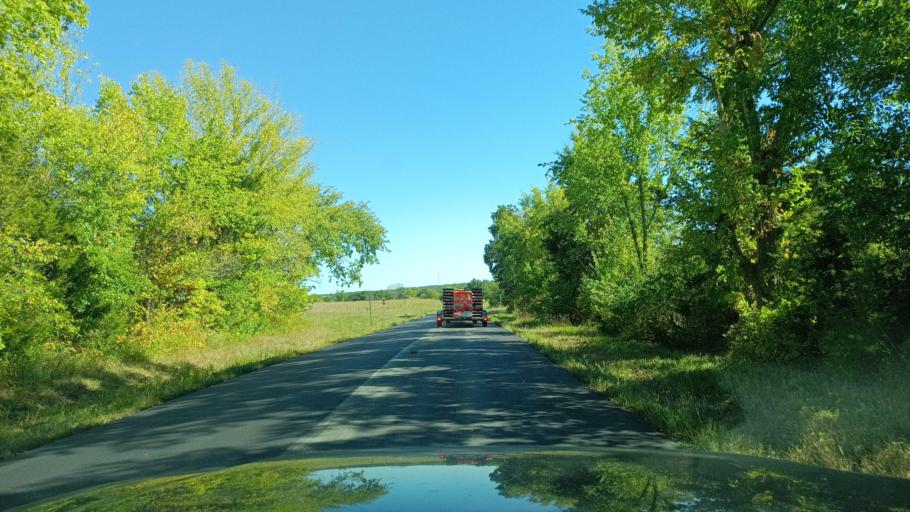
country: US
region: Missouri
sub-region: Macon County
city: La Plata
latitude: 39.9226
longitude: -92.5331
